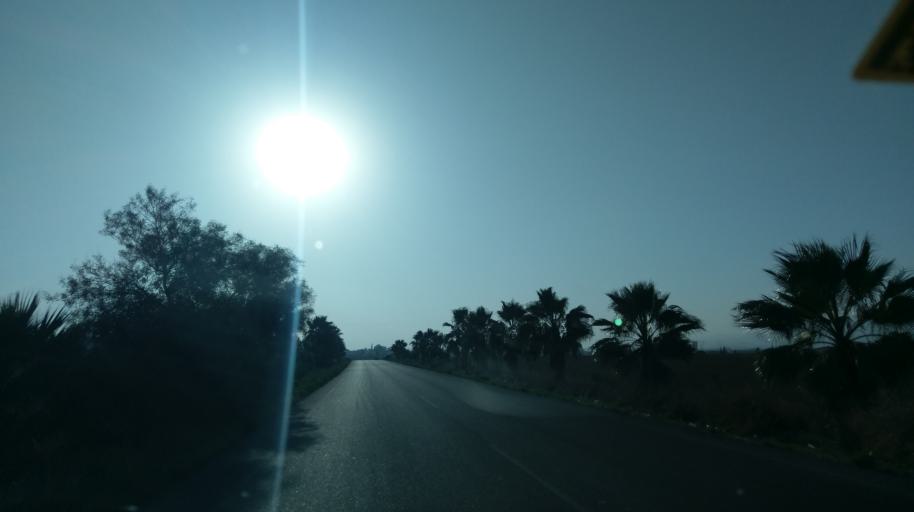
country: CY
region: Ammochostos
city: Leonarisso
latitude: 35.3749
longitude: 34.0418
